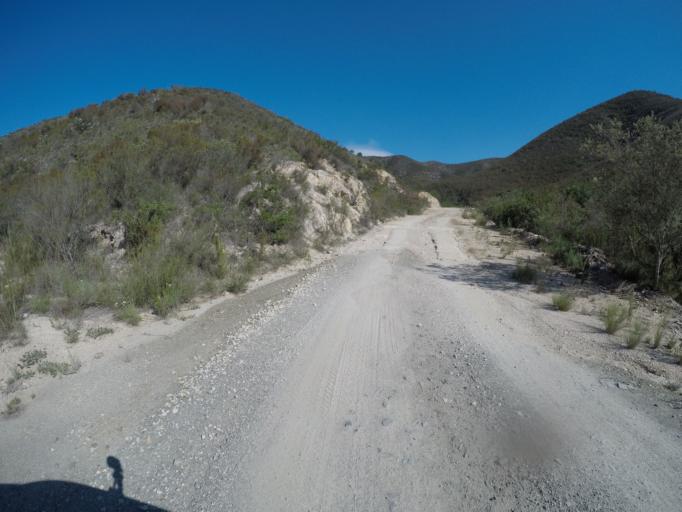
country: ZA
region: Eastern Cape
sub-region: Cacadu District Municipality
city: Kareedouw
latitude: -33.6536
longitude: 24.4991
